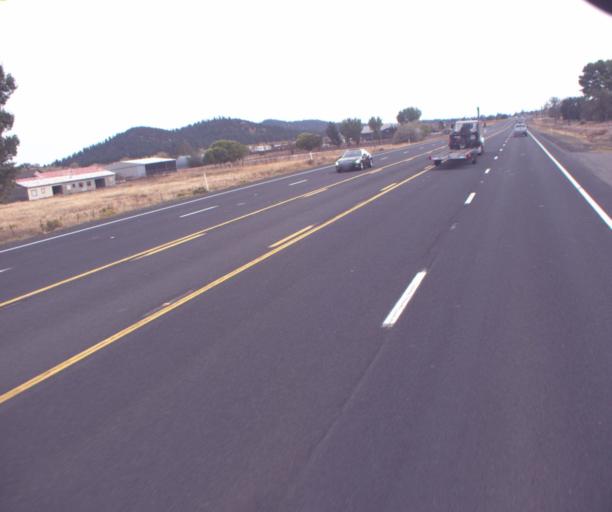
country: US
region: Arizona
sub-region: Coconino County
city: Flagstaff
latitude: 35.3110
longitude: -111.5427
